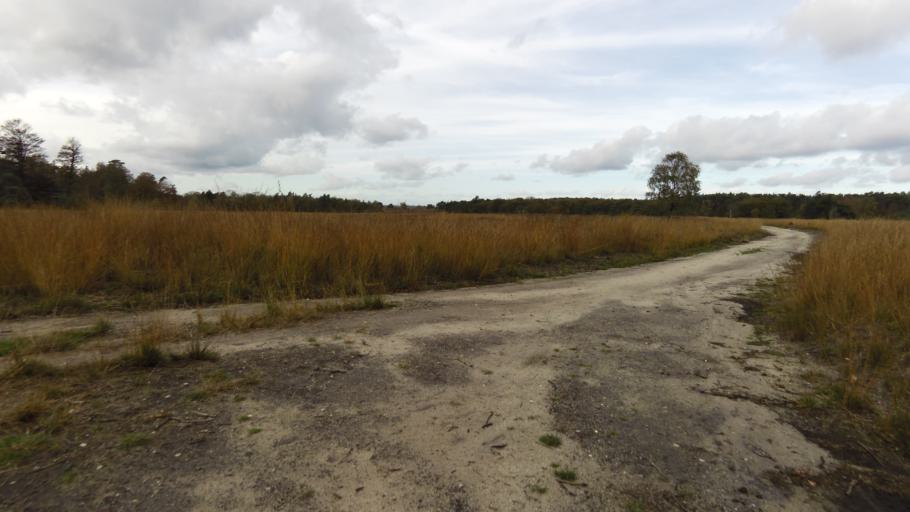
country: NL
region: Gelderland
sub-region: Gemeente Apeldoorn
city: Uddel
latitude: 52.3010
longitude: 5.8258
